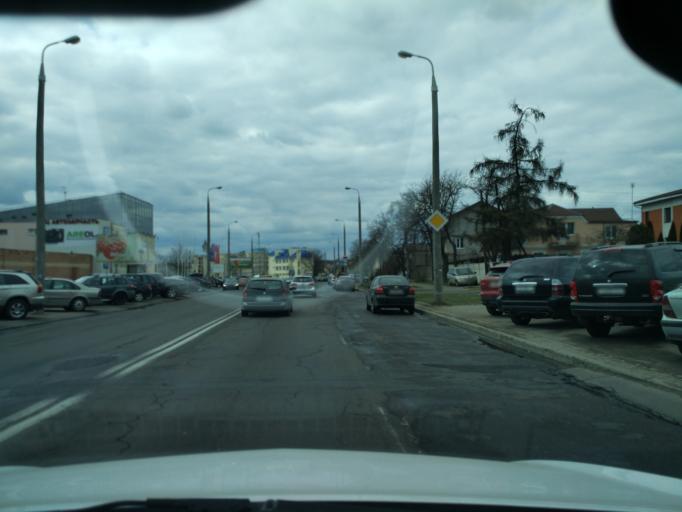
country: BY
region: Minsk
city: Minsk
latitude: 53.9377
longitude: 27.5778
